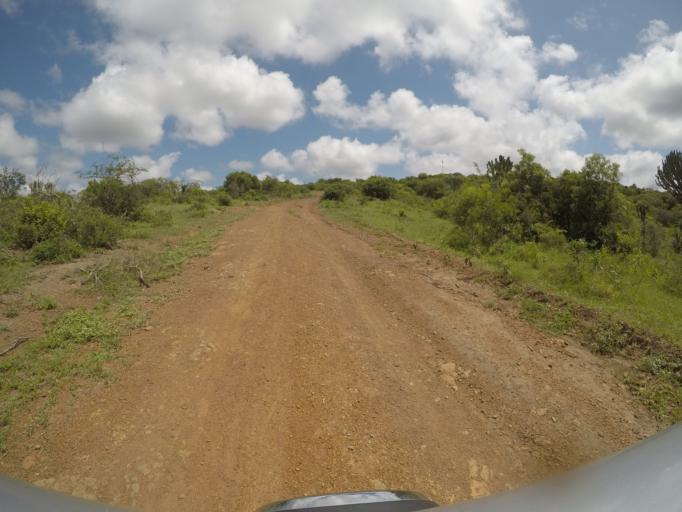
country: ZA
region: KwaZulu-Natal
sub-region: uThungulu District Municipality
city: Empangeni
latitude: -28.5852
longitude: 31.8278
